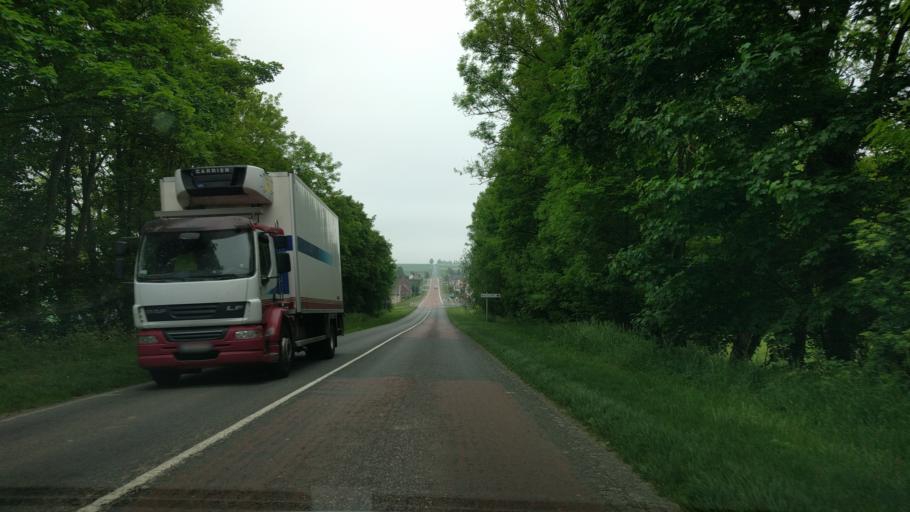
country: FR
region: Picardie
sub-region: Departement de la Somme
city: Moislains
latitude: 49.9790
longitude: 2.9177
